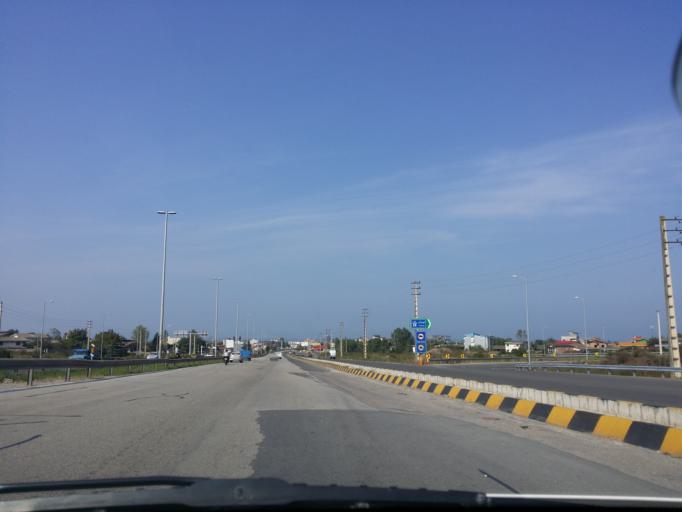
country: IR
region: Mazandaran
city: Chalus
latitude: 36.6536
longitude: 51.4043
